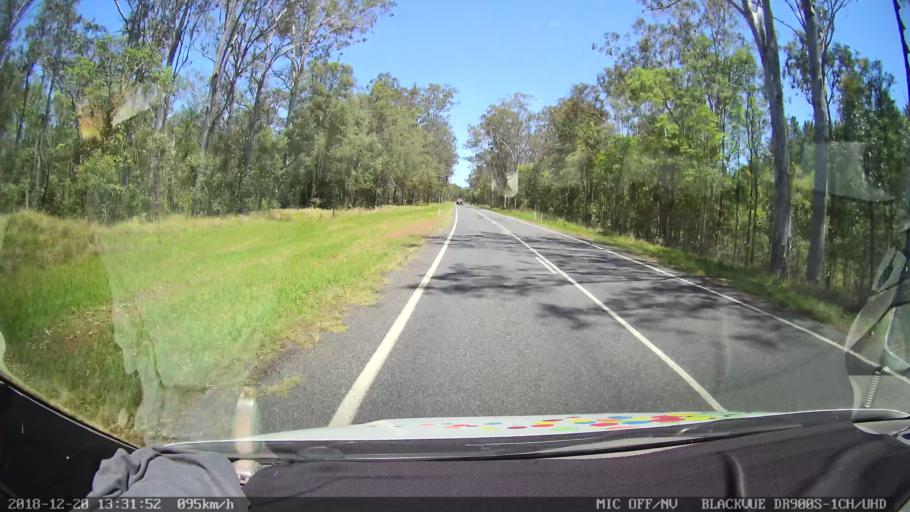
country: AU
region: New South Wales
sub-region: Clarence Valley
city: Gordon
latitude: -29.2240
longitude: 152.9875
